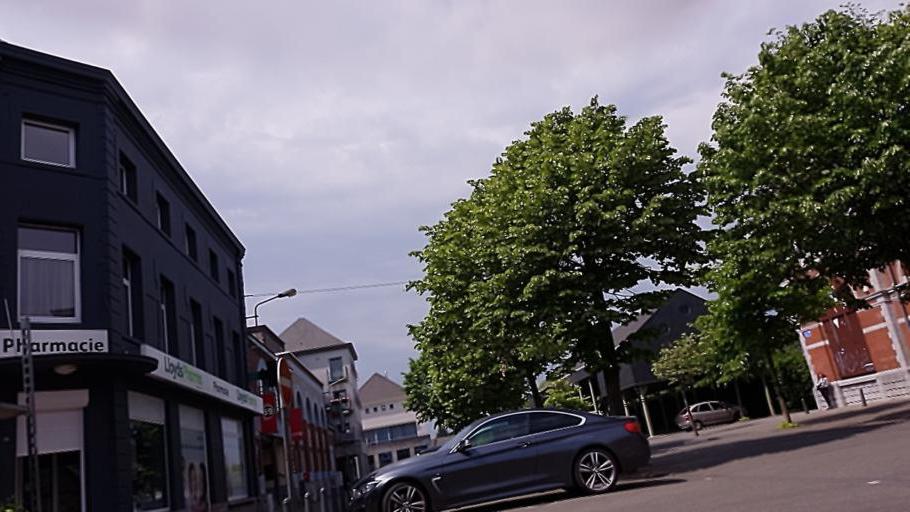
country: BE
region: Wallonia
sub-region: Province du Hainaut
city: Peruwelz
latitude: 50.5132
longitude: 3.5919
